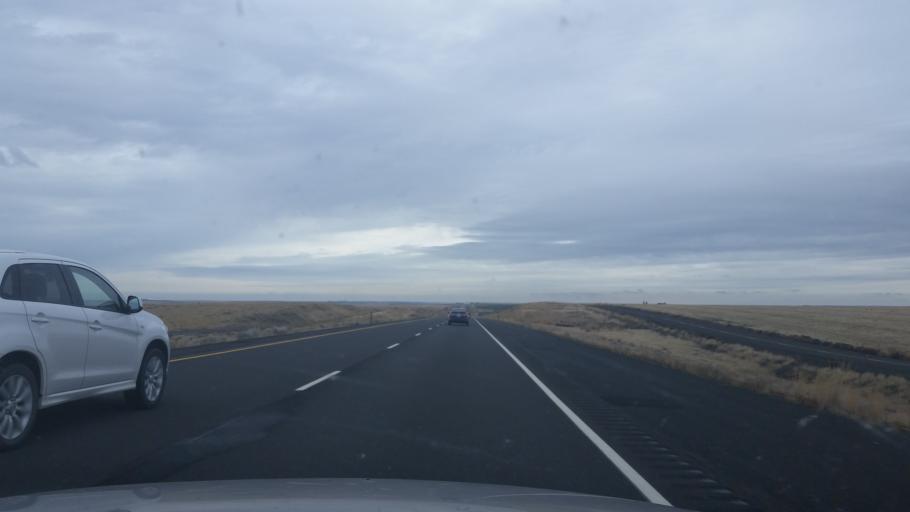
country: US
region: Washington
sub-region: Grant County
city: Warden
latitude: 47.0866
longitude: -118.7253
